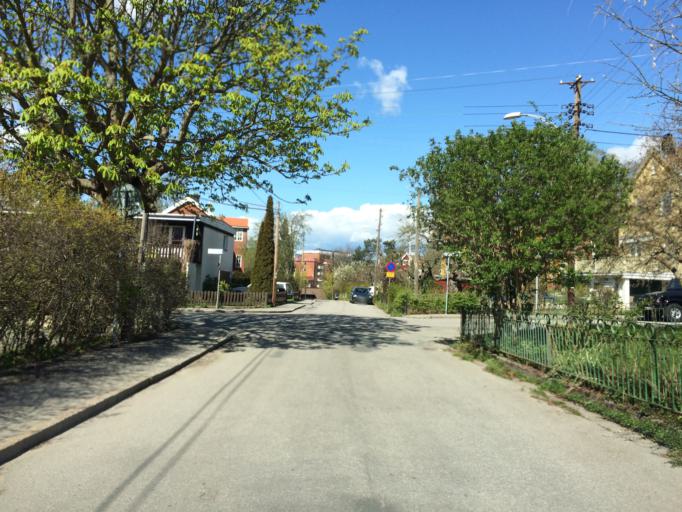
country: SE
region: Stockholm
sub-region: Huddinge Kommun
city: Segeltorp
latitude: 59.3015
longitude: 17.9745
